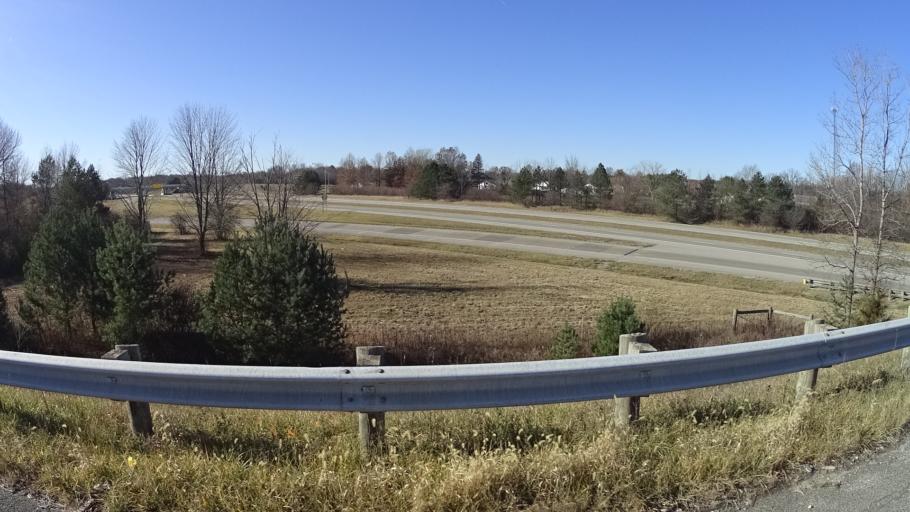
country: US
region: Ohio
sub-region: Lorain County
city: Oberlin
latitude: 41.2938
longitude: -82.1667
